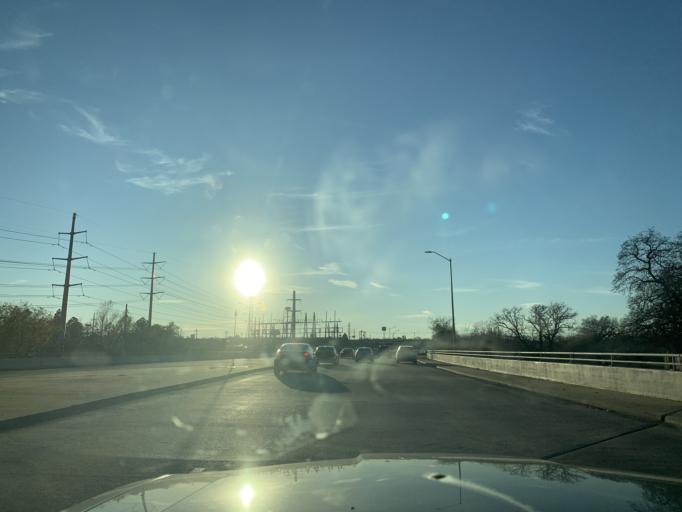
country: US
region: Texas
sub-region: Tarrant County
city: Euless
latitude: 32.8668
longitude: -97.0970
